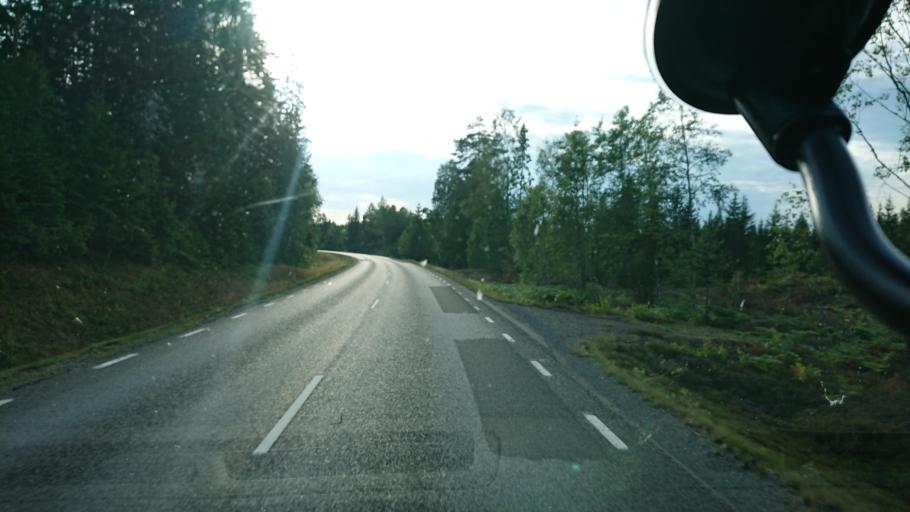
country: SE
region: Kronoberg
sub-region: Vaxjo Kommun
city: Braas
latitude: 57.0245
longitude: 15.0036
